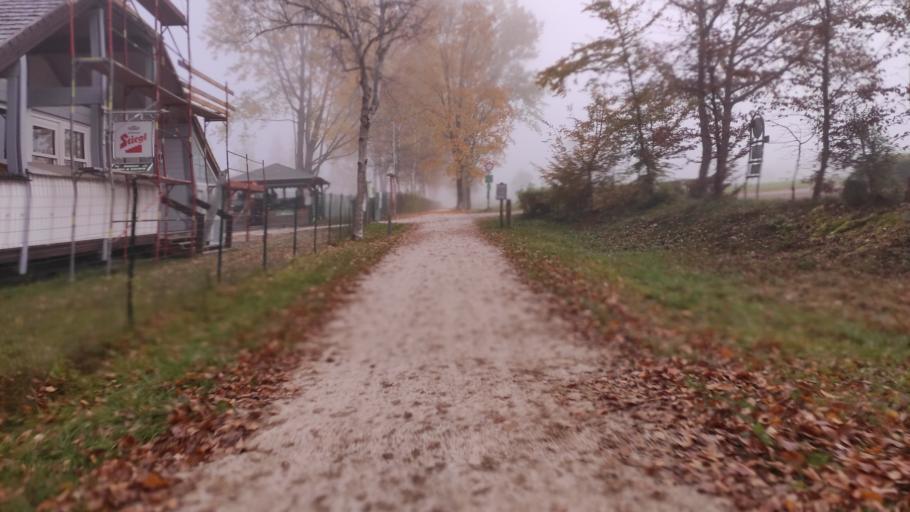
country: AT
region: Upper Austria
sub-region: Politischer Bezirk Gmunden
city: Sankt Wolfgang im Salzkammergut
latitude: 47.7162
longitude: 13.4532
